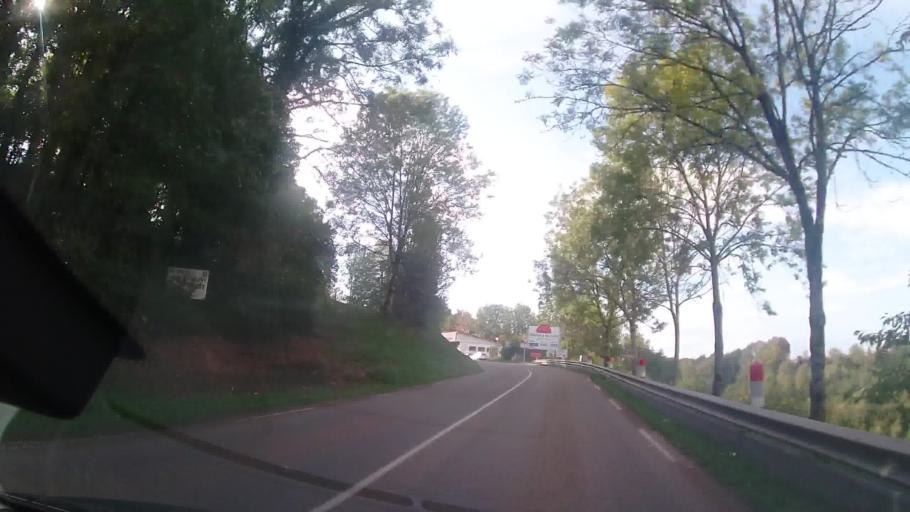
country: FR
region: Franche-Comte
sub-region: Departement du Jura
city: Clairvaux-les-Lacs
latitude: 46.5761
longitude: 5.7550
